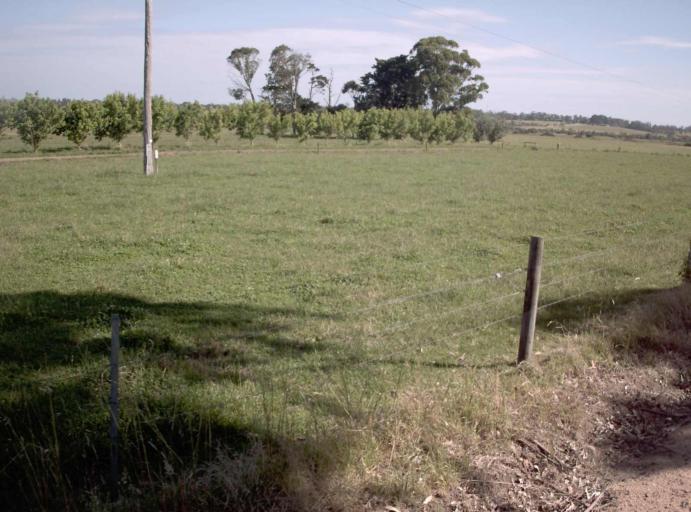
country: AU
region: Victoria
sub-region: East Gippsland
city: Lakes Entrance
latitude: -37.7659
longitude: 148.5384
